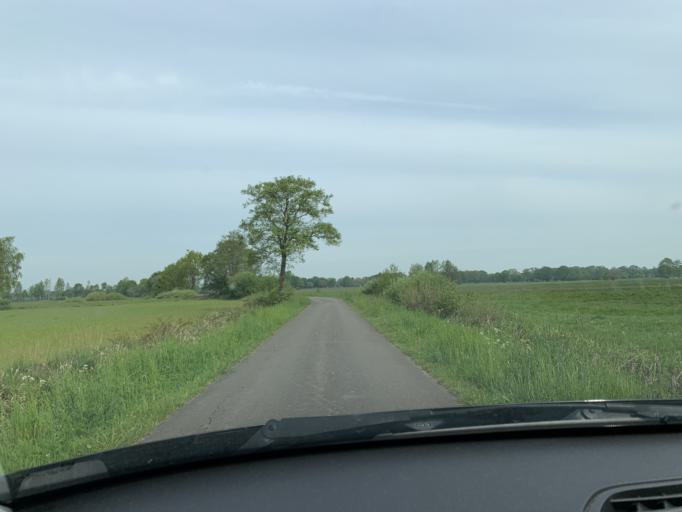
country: DE
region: Lower Saxony
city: Apen
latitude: 53.2381
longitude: 7.8318
